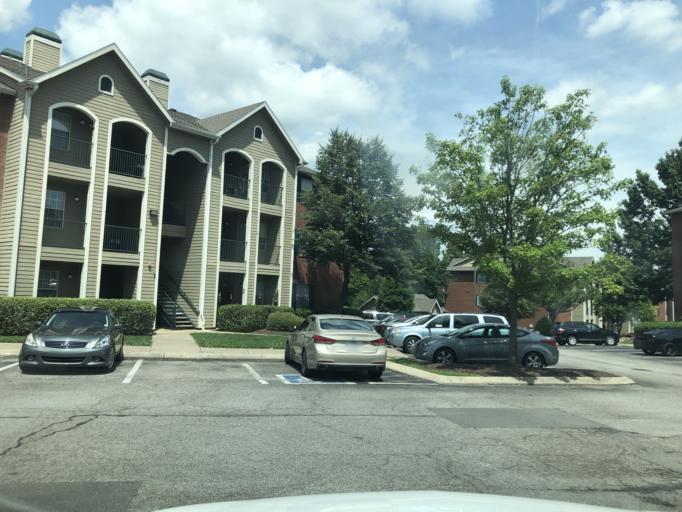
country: US
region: Tennessee
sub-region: Rutherford County
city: La Vergne
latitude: 36.0367
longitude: -86.6384
